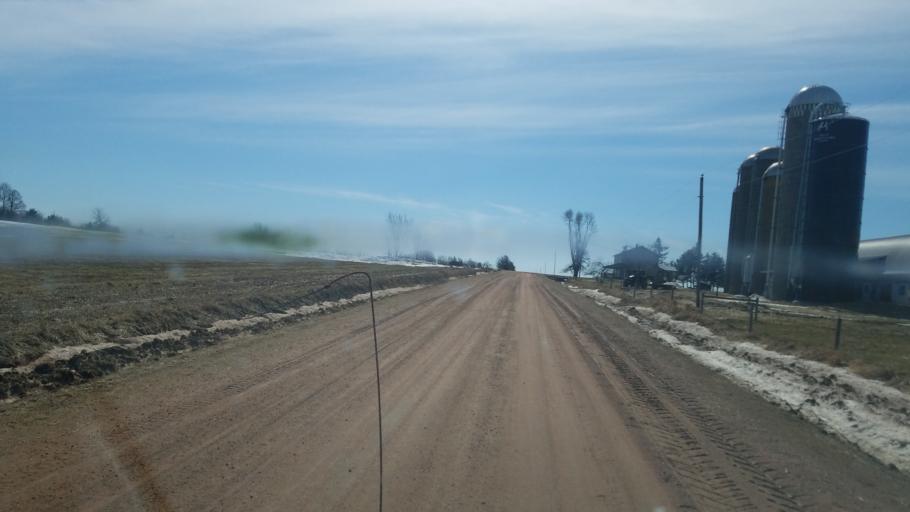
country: US
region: Wisconsin
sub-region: Clark County
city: Loyal
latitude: 44.6167
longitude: -90.4273
